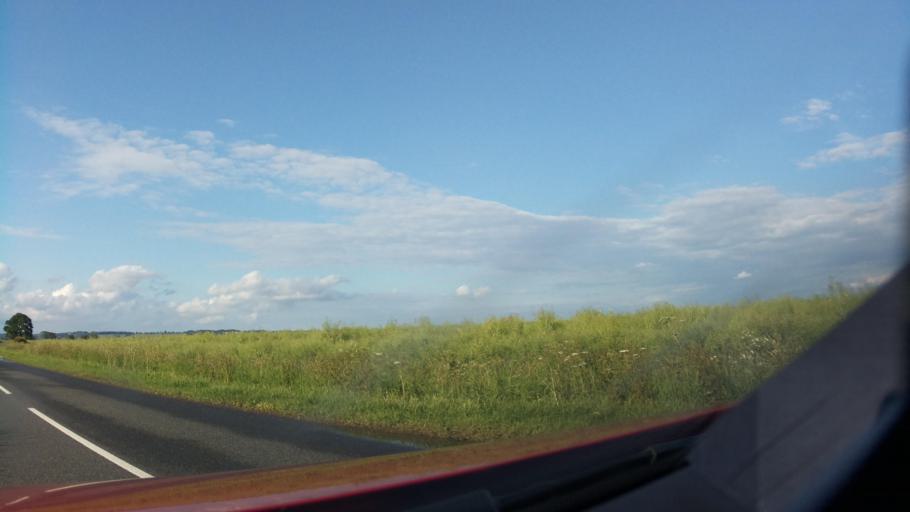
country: GB
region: England
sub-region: Lincolnshire
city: Navenby
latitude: 53.1037
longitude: -0.6076
